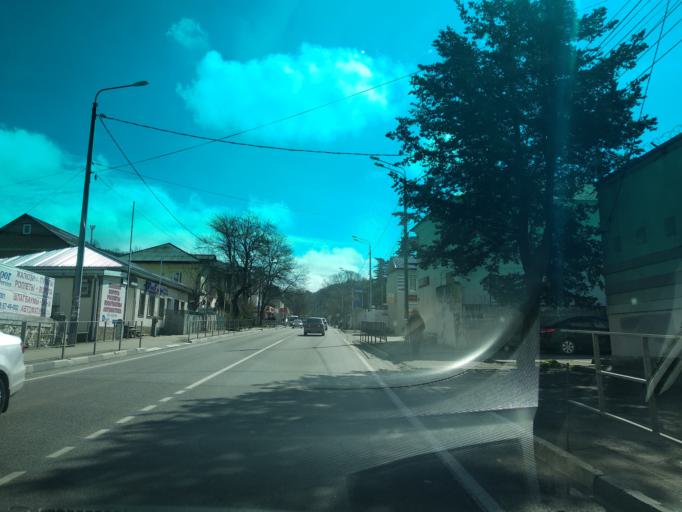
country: RU
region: Krasnodarskiy
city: Tuapse
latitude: 44.0992
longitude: 39.0964
